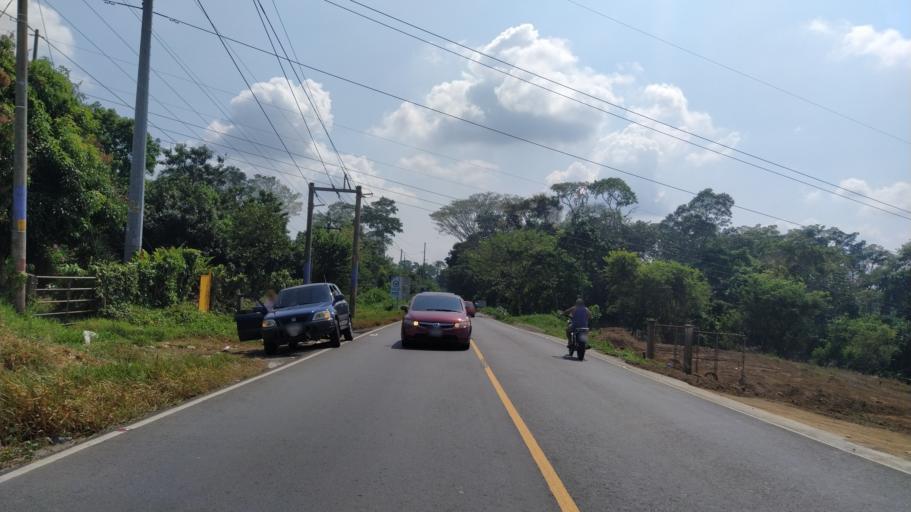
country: GT
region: Retalhuleu
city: San Felipe
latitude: 14.6278
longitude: -91.5859
